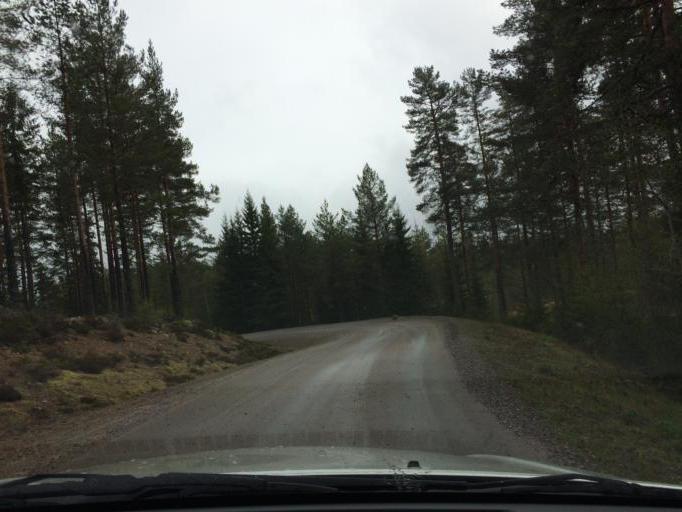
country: SE
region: OErebro
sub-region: Hallefors Kommun
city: Haellefors
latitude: 60.0155
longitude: 14.5880
